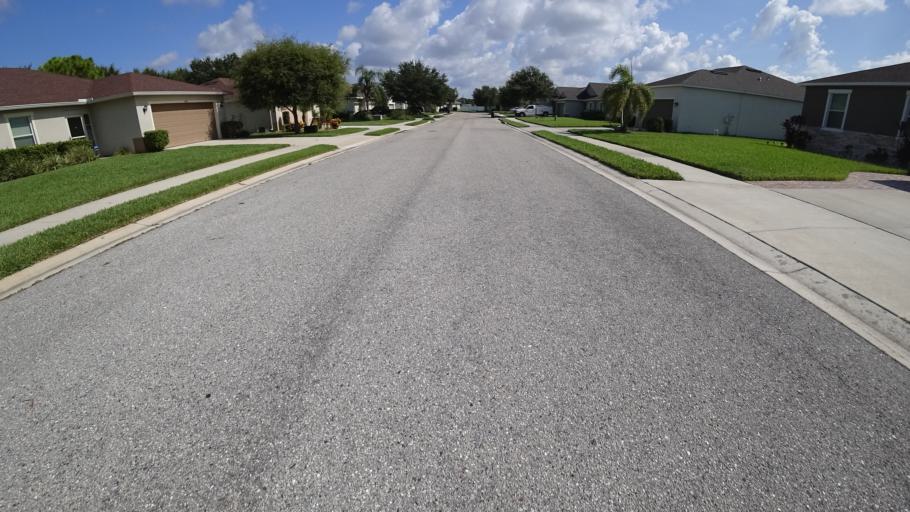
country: US
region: Florida
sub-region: Manatee County
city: Whitfield
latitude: 27.4264
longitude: -82.5625
